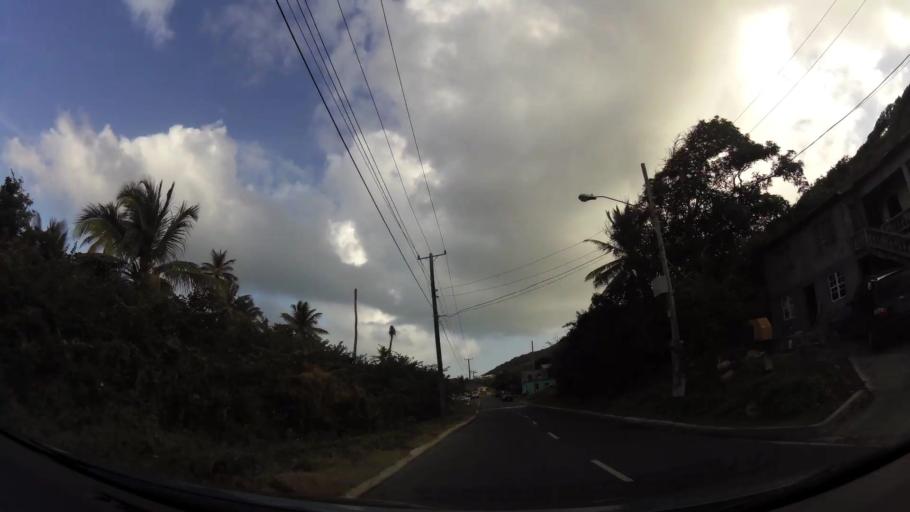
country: KN
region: Saint James Windwa
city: Newcastle
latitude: 17.1952
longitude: -62.5694
